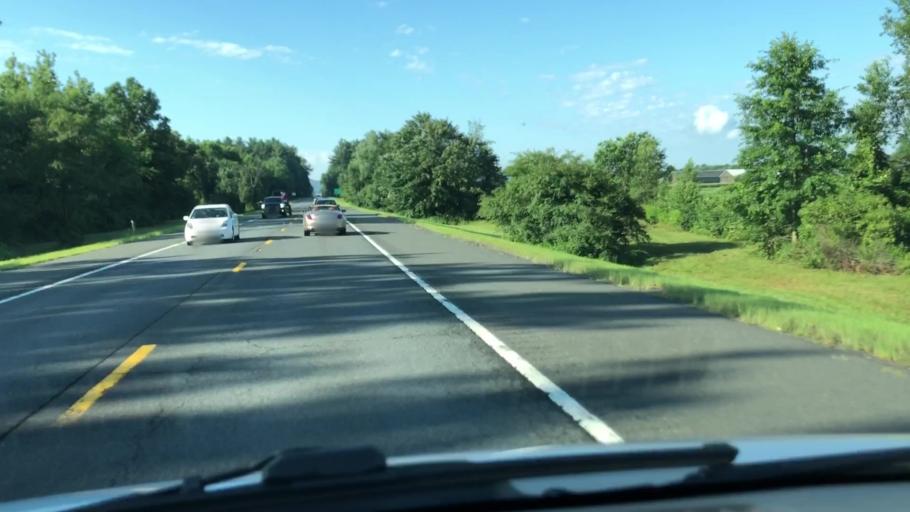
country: US
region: Massachusetts
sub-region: Hampshire County
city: North Amherst
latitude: 42.4044
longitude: -72.5386
